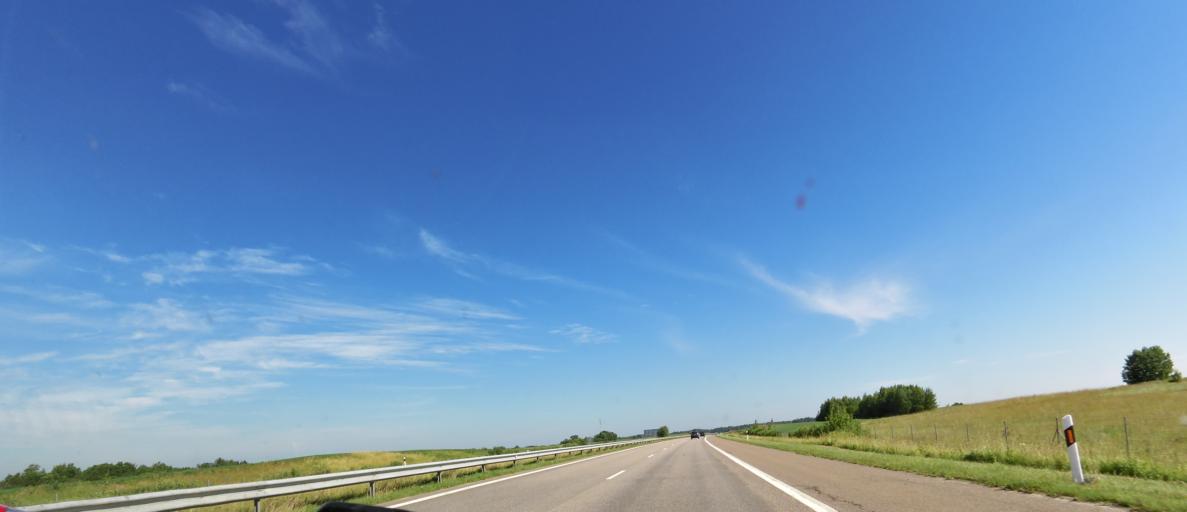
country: LT
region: Vilnius County
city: Ukmerge
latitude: 55.1867
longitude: 24.8113
